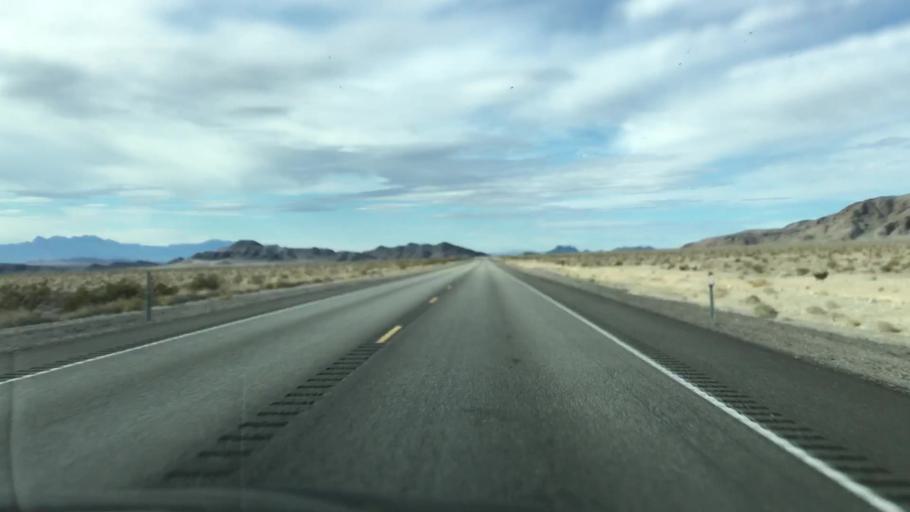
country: US
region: Nevada
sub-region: Nye County
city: Pahrump
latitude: 36.5709
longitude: -116.1663
